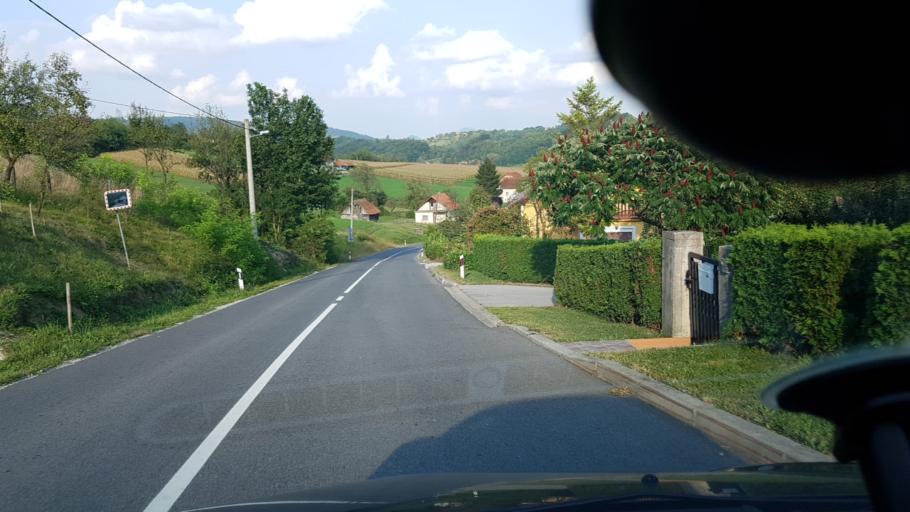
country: HR
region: Krapinsko-Zagorska
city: Pregrada
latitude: 46.1501
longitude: 15.6824
